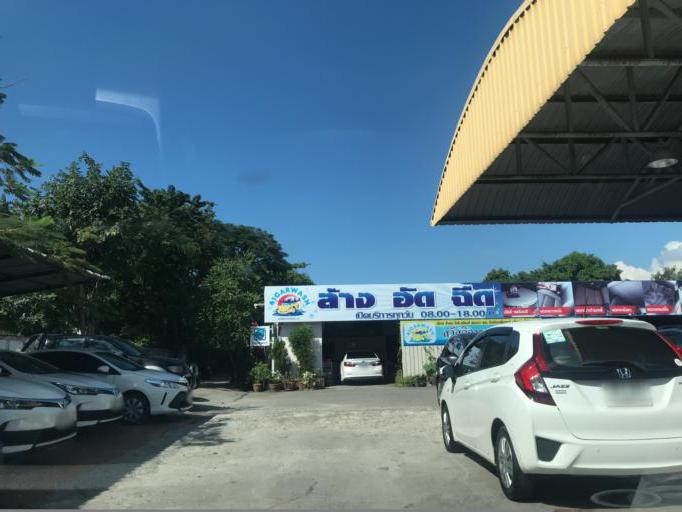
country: TH
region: Chiang Mai
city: Chiang Mai
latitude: 18.7722
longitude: 98.9716
